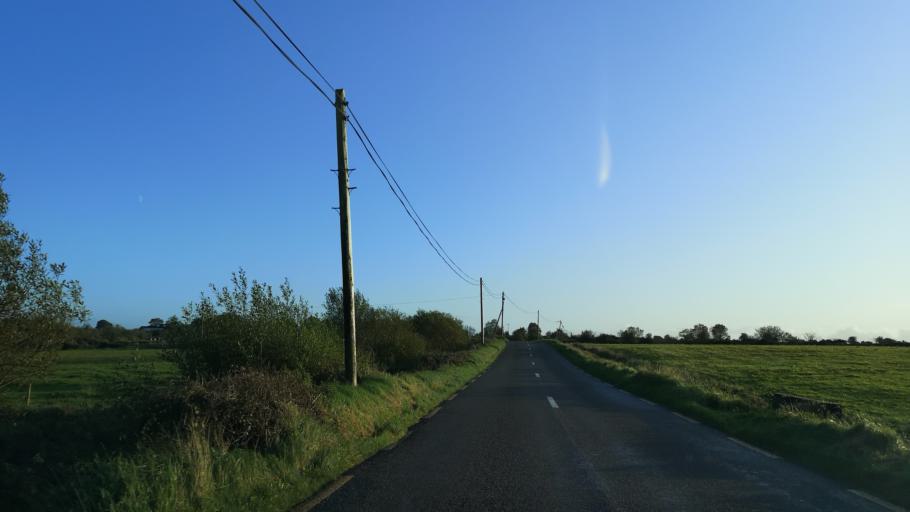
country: IE
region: Connaught
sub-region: Roscommon
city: Castlerea
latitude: 53.7050
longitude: -8.5657
